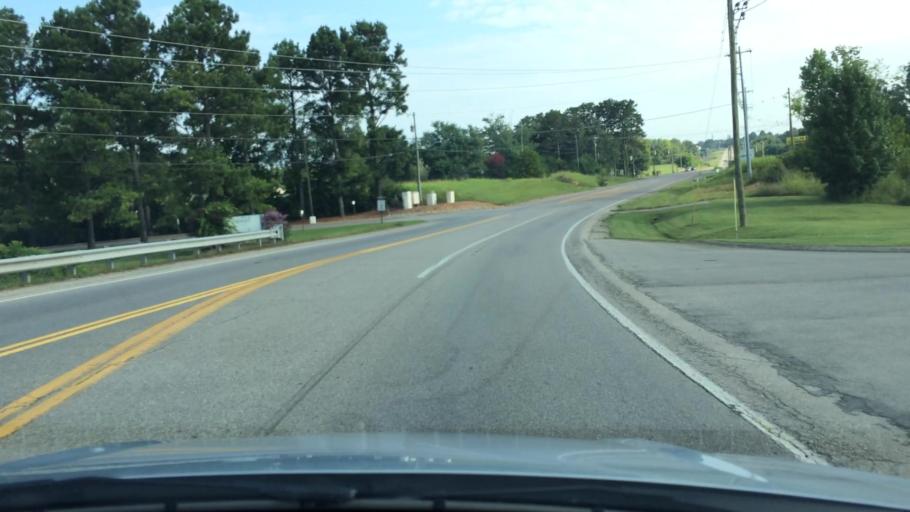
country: US
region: Tennessee
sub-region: Blount County
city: Maryville
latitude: 35.7427
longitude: -84.0442
